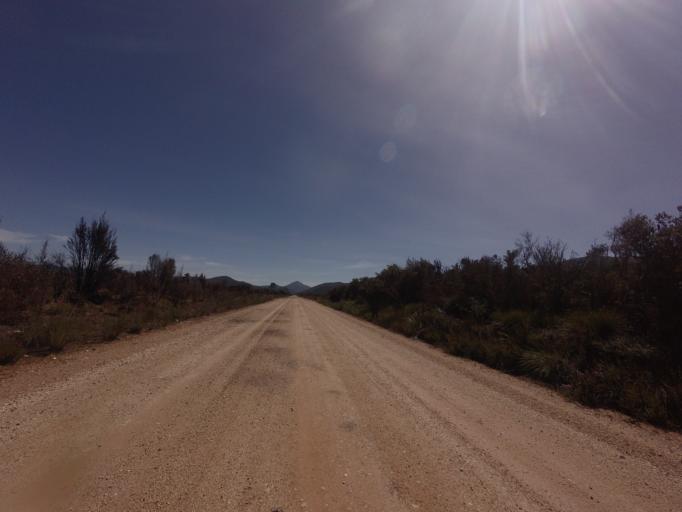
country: AU
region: Tasmania
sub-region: Huon Valley
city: Geeveston
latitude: -42.9724
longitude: 146.3649
